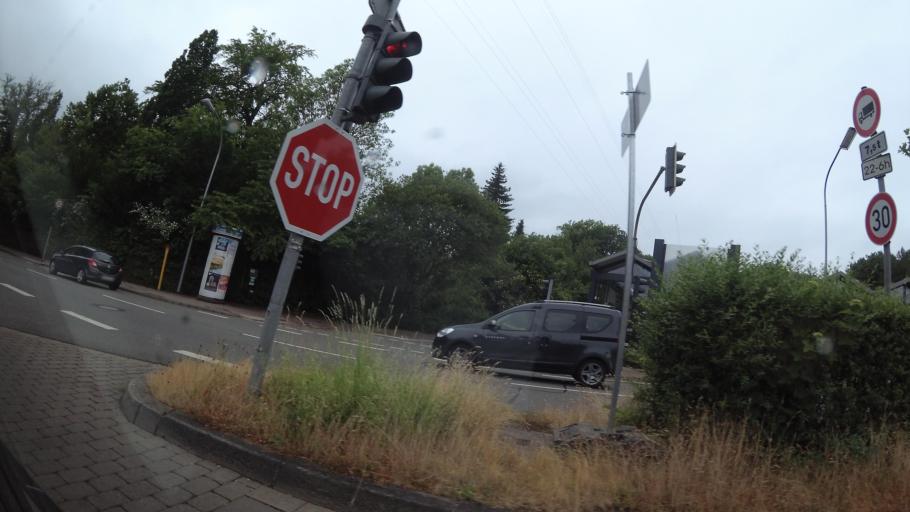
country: DE
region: Saarland
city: Saarbrucken
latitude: 49.2531
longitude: 6.9543
